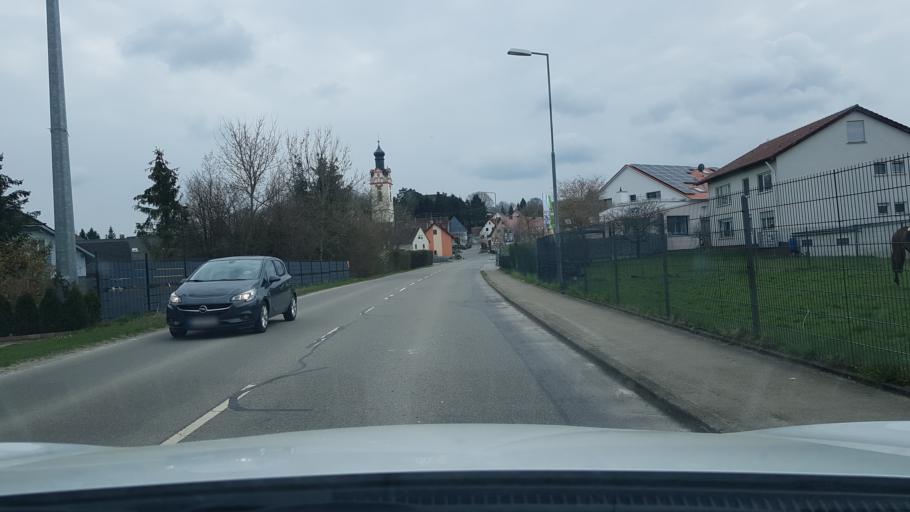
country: DE
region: Baden-Wuerttemberg
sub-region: Tuebingen Region
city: Oberstadion
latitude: 48.1887
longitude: 9.6912
